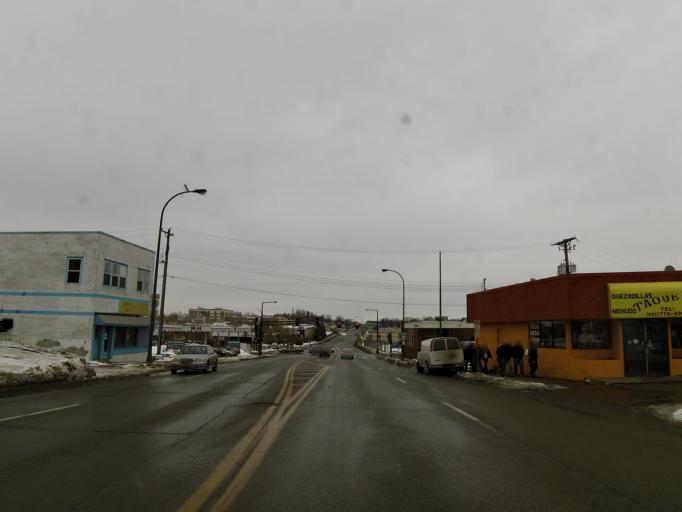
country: US
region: Minnesota
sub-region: Ramsey County
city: Saint Paul
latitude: 44.9622
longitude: -93.0659
